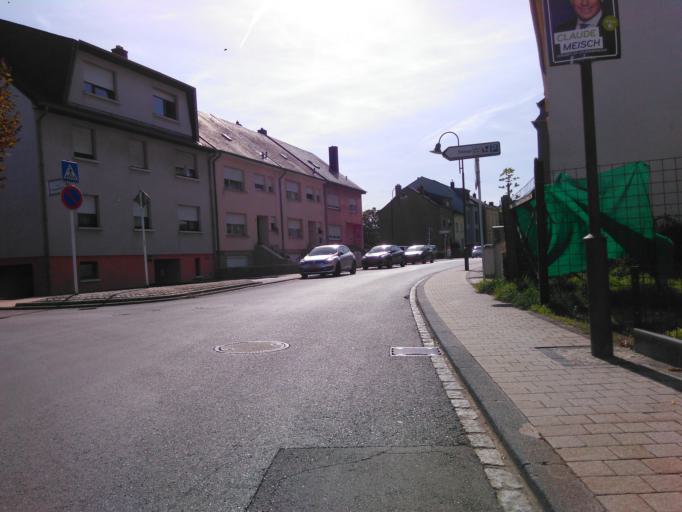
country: LU
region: Luxembourg
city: Tetange
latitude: 49.4765
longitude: 6.0355
